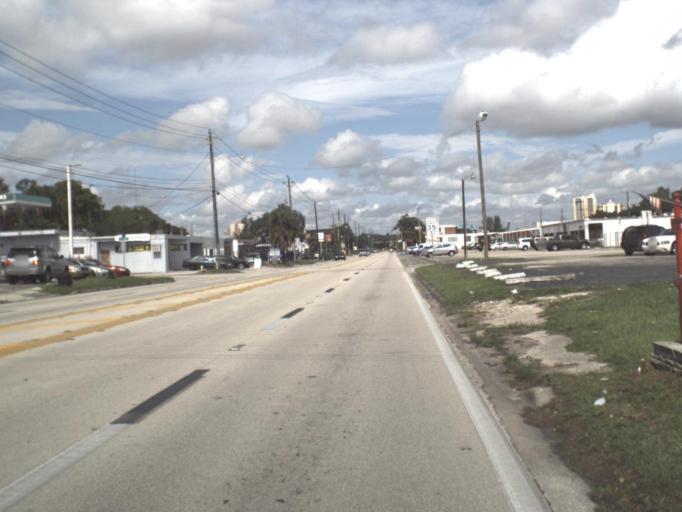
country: US
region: Florida
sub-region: Lee County
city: Fort Myers
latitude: 26.6340
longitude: -81.8622
